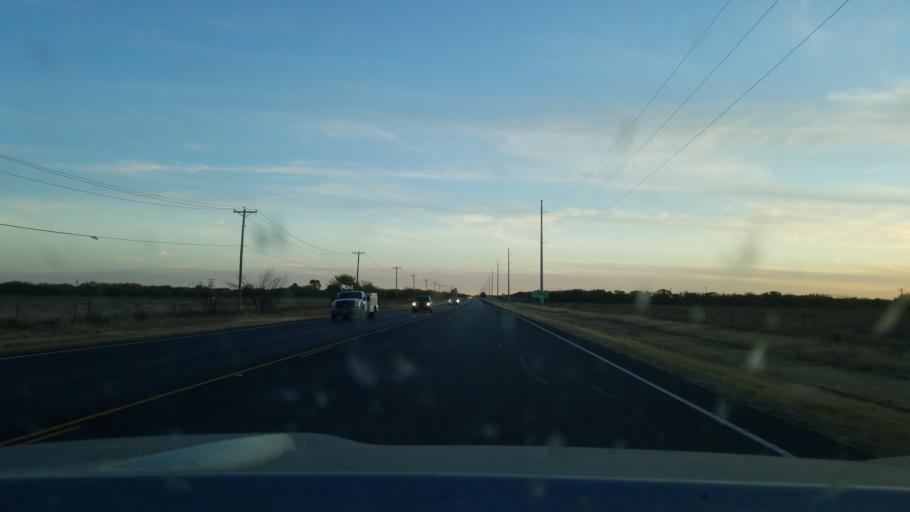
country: US
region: Texas
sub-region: Stephens County
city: Breckenridge
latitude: 32.7296
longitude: -98.9027
